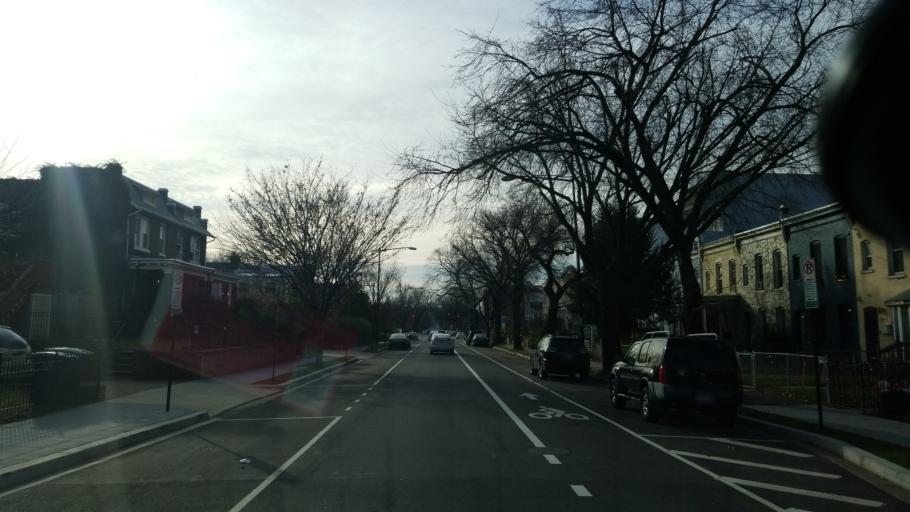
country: US
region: Washington, D.C.
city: Washington, D.C.
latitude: 38.8875
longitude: -76.9808
